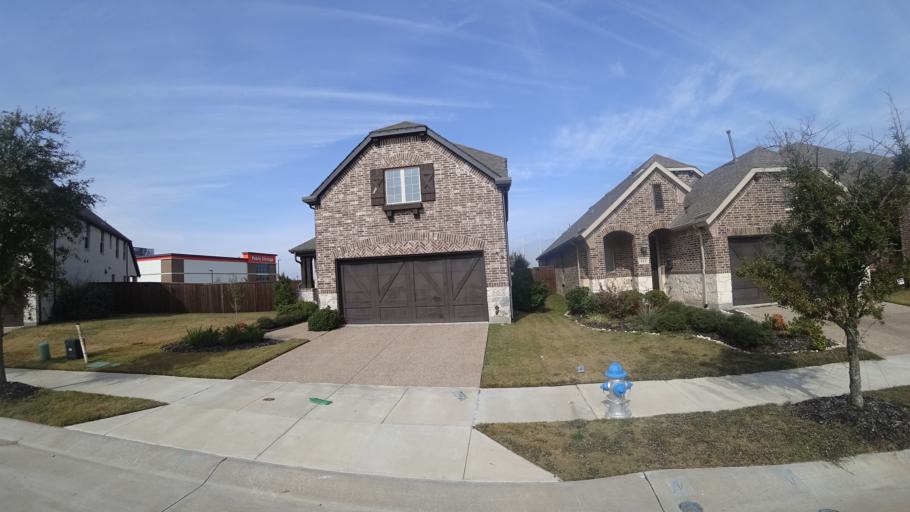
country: US
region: Texas
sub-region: Denton County
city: The Colony
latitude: 33.0671
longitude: -96.8803
